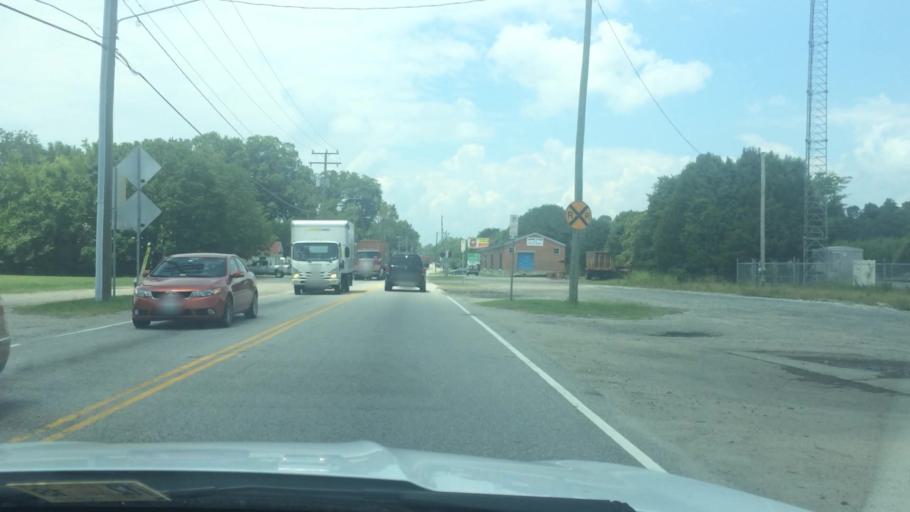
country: US
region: Virginia
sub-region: York County
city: Yorktown
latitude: 37.1937
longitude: -76.5731
